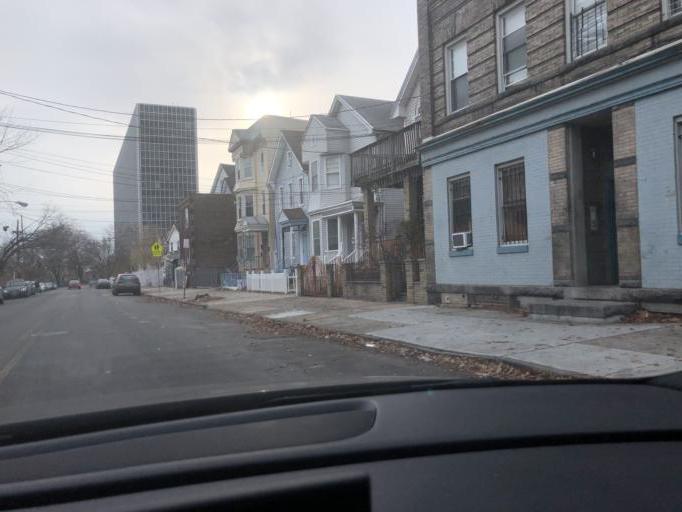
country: US
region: New Jersey
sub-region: Hudson County
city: East Newark
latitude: 40.7528
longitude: -74.1780
